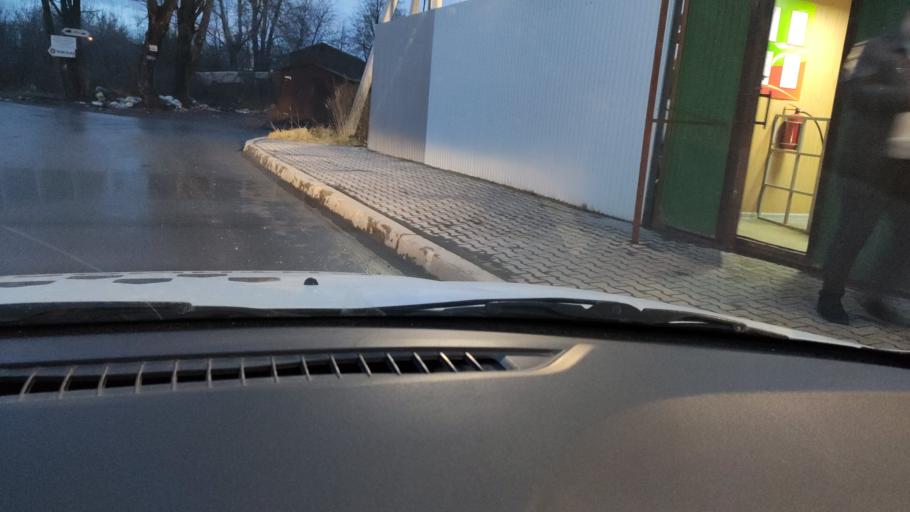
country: RU
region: Perm
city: Kondratovo
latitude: 58.0041
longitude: 56.1415
